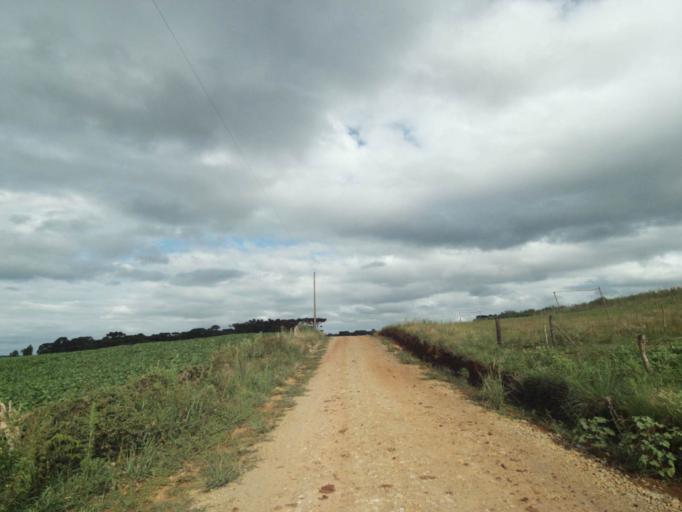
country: BR
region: Rio Grande do Sul
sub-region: Lagoa Vermelha
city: Lagoa Vermelha
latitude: -28.2032
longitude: -51.5112
